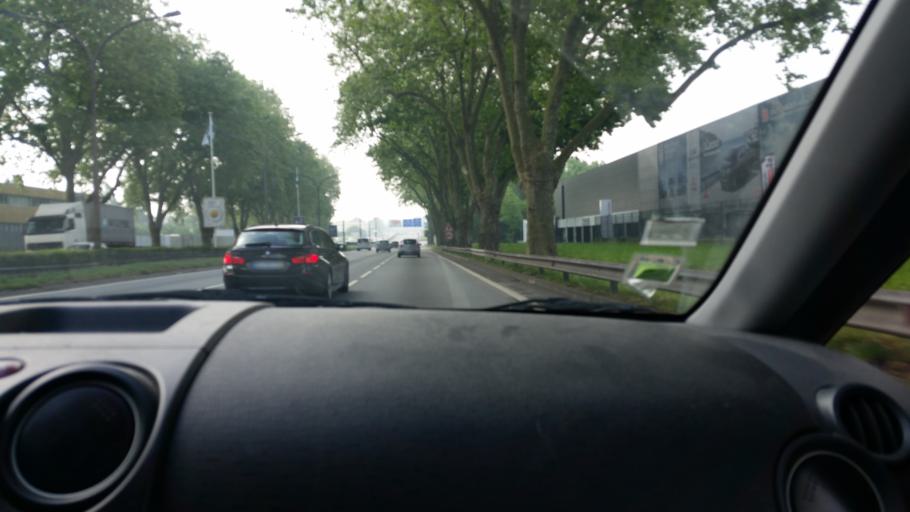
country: PT
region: Porto
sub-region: Matosinhos
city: Senhora da Hora
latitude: 41.1705
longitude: -8.6466
